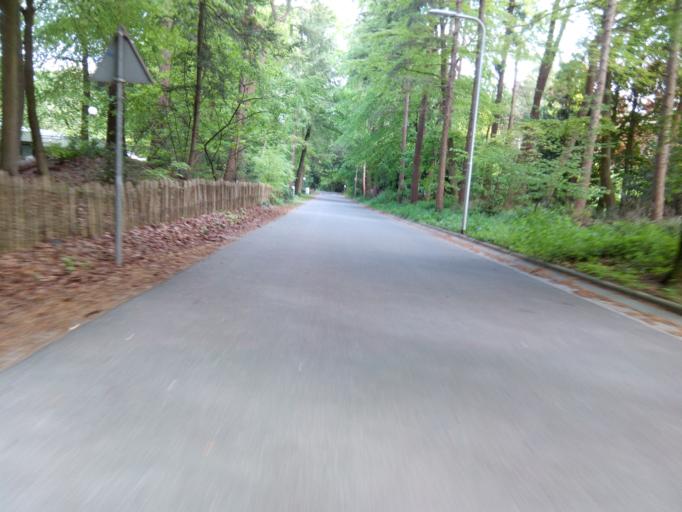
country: NL
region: Gelderland
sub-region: Gemeente Ede
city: Lunteren
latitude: 52.0846
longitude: 5.6357
